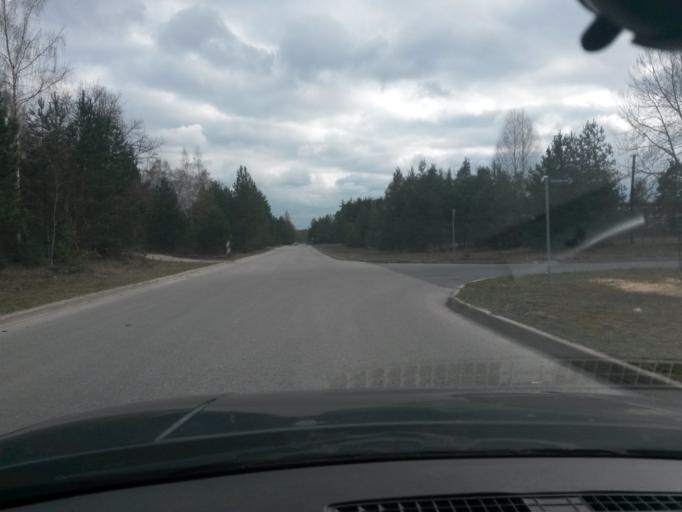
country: LV
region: Stopini
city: Ulbroka
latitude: 56.9025
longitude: 24.2468
